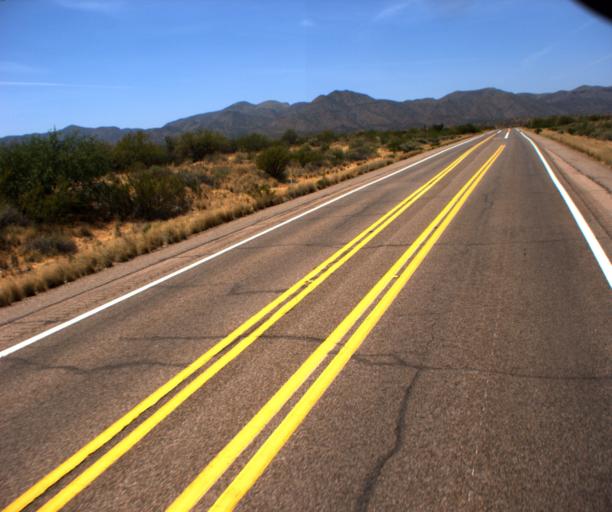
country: US
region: Arizona
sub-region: Gila County
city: Miami
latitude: 33.6161
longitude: -111.0394
